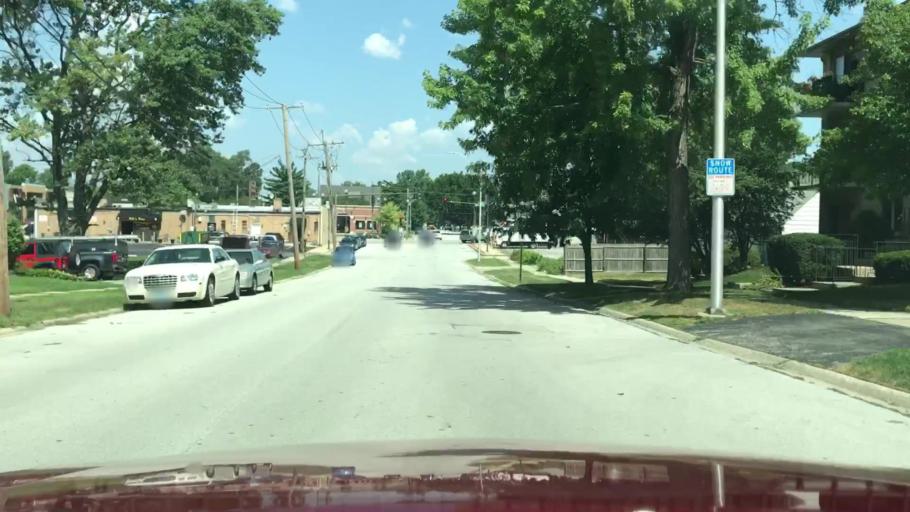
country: US
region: Illinois
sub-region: Cook County
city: Oak Lawn
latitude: 41.7186
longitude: -87.7555
